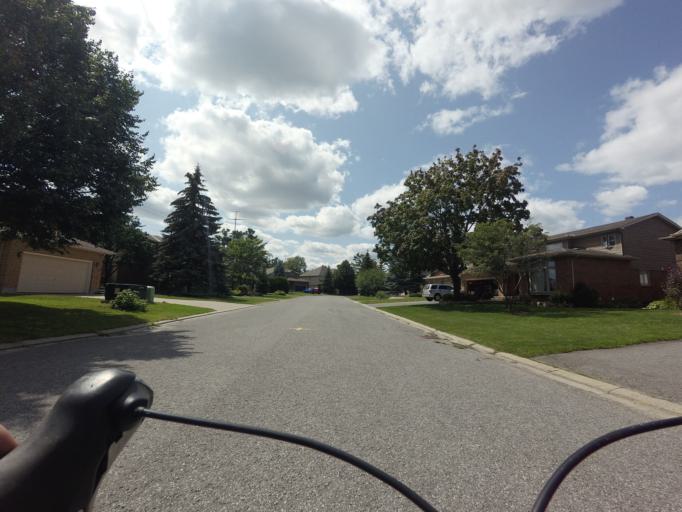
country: CA
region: Ontario
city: Bells Corners
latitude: 45.2905
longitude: -75.8488
